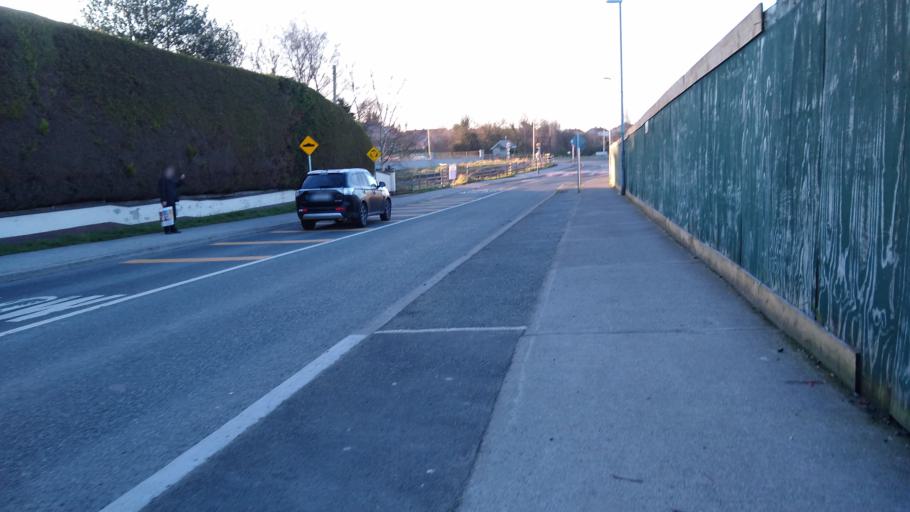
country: IE
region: Leinster
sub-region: An Mhi
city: Ashbourne
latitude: 53.5110
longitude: -6.4048
